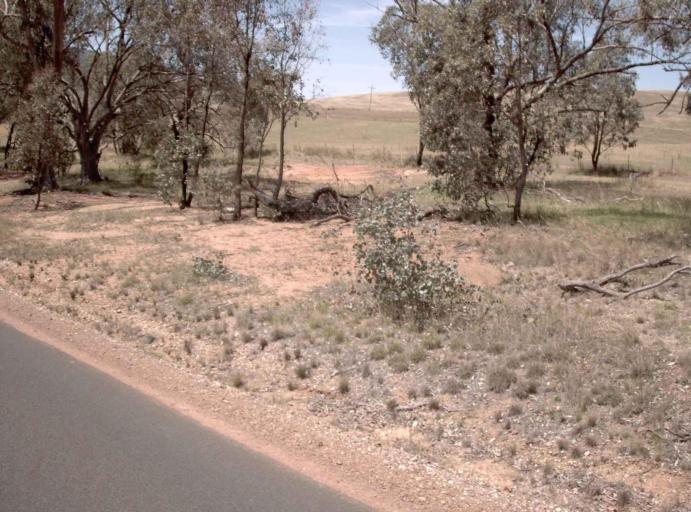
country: AU
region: Victoria
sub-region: East Gippsland
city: Bairnsdale
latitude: -37.1842
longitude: 147.7149
